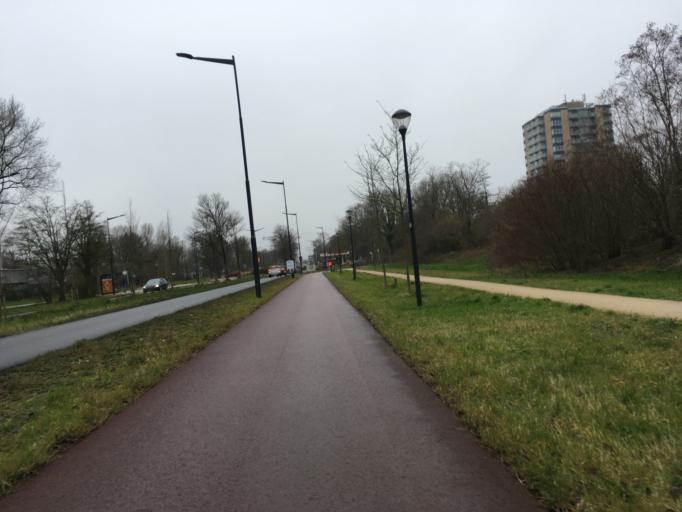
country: NL
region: North Holland
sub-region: Gemeente Heemstede
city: Heemstede
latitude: 52.3551
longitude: 4.6464
